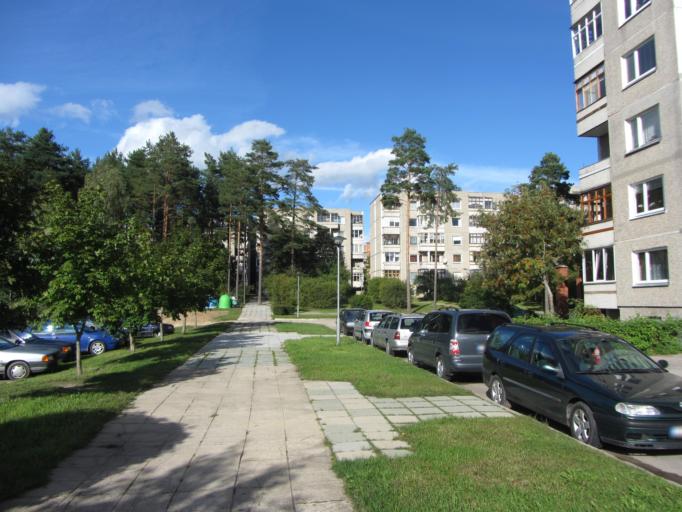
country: LT
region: Utenos apskritis
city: Visaginas
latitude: 55.5878
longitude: 26.4477
